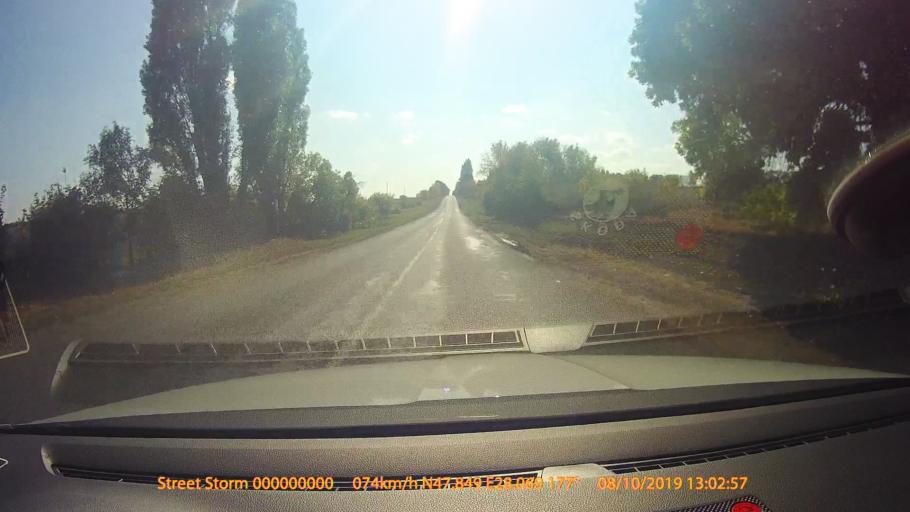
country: MD
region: Singerei
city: Biruinta
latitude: 47.8485
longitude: 28.0695
